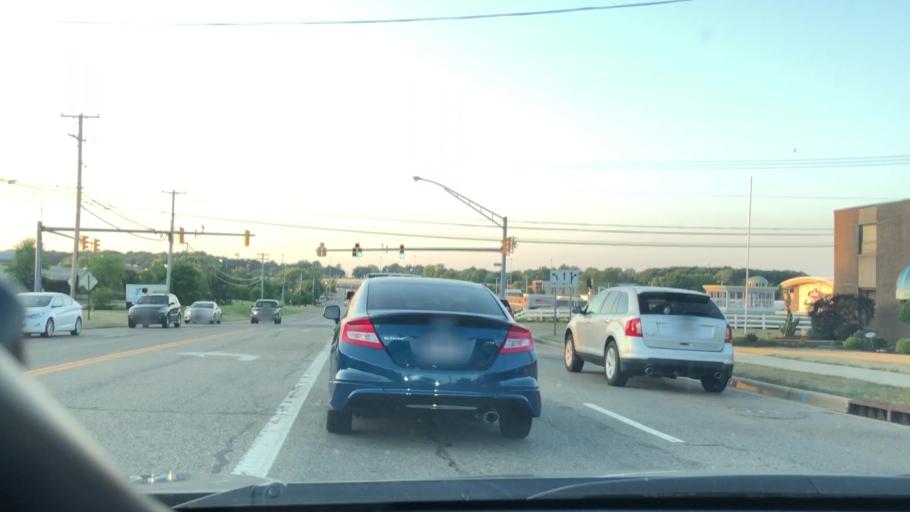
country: US
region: Ohio
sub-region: Summit County
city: Green
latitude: 40.9551
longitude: -81.4657
